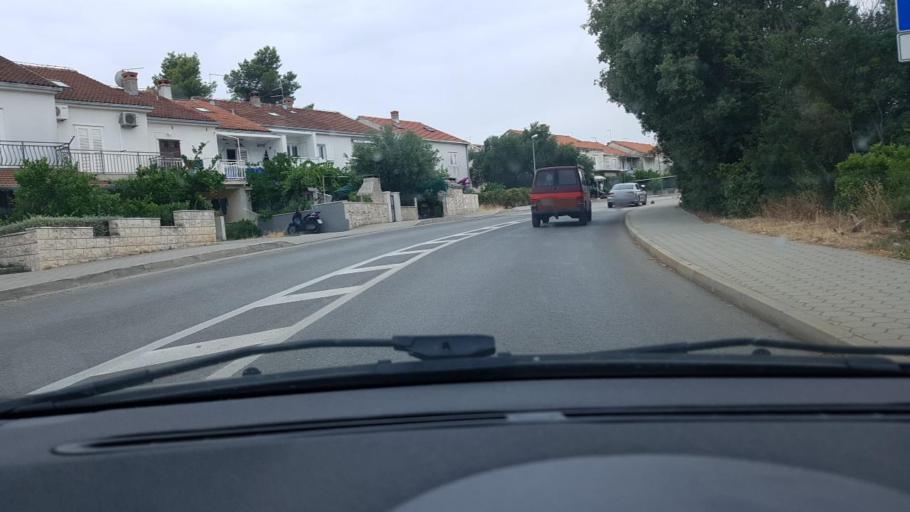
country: HR
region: Dubrovacko-Neretvanska
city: Korcula
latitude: 42.9503
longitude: 17.1449
